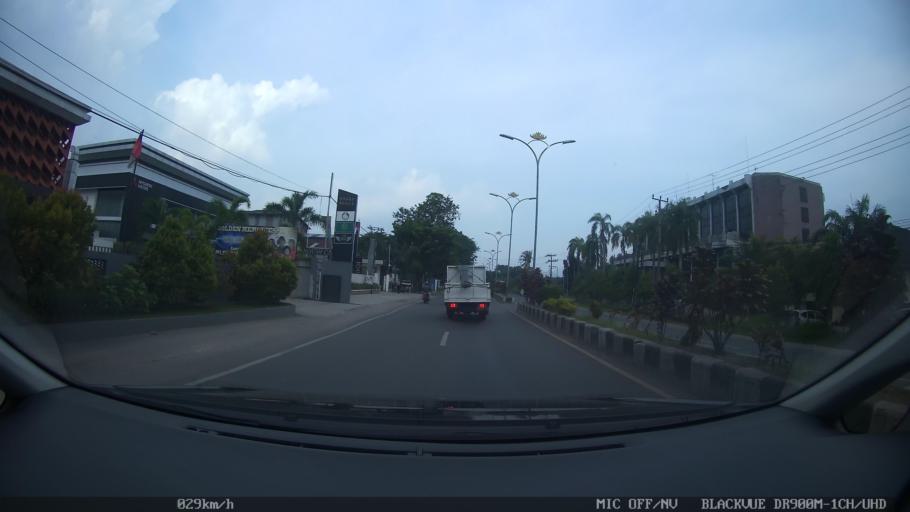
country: ID
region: Lampung
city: Panjang
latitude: -5.4450
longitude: 105.2956
